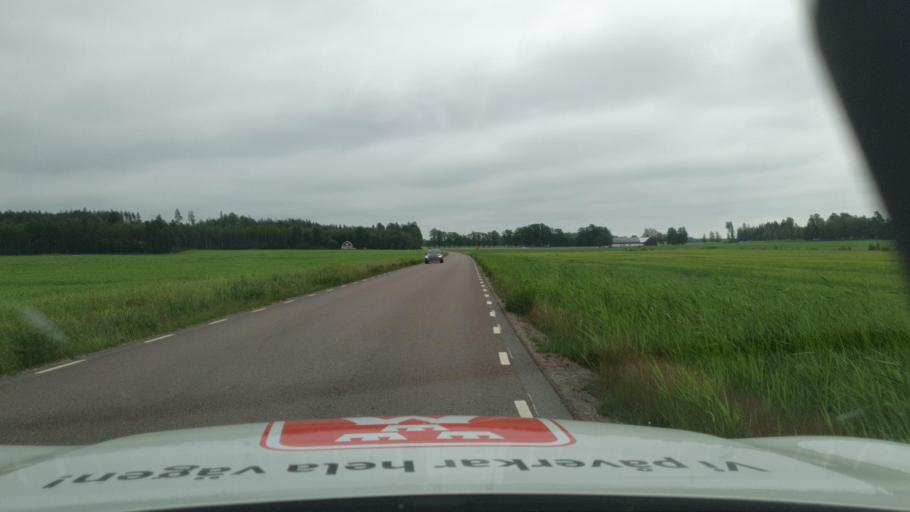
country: SE
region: Vaermland
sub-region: Karlstads Kommun
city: Skattkarr
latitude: 59.4131
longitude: 13.8754
